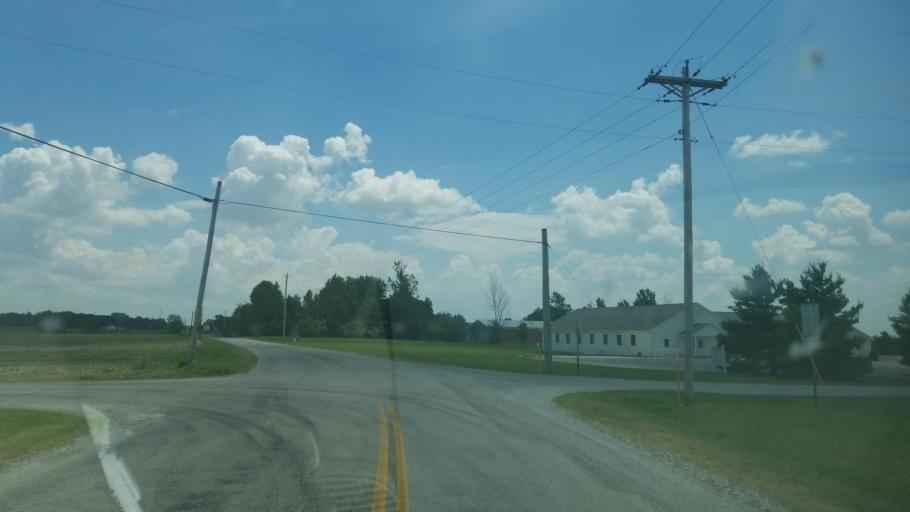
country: US
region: Ohio
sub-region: Hardin County
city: Kenton
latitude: 40.6609
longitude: -83.6552
